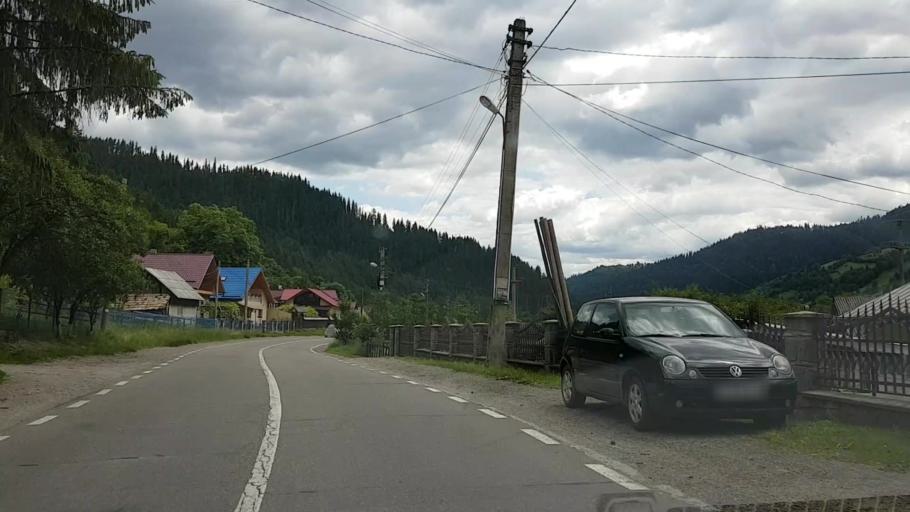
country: RO
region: Neamt
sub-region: Comuna Poiana Teiului
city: Poiana Teiului
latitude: 47.1310
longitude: 25.8995
